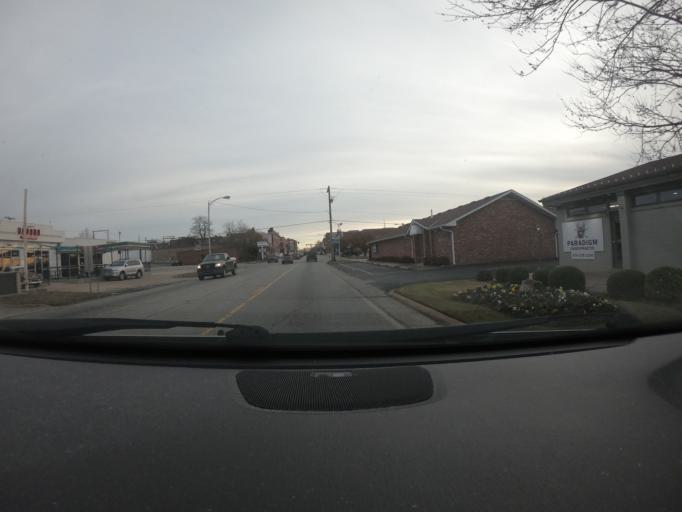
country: US
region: Arkansas
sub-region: Benton County
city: Rogers
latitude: 36.3348
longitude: -94.1172
